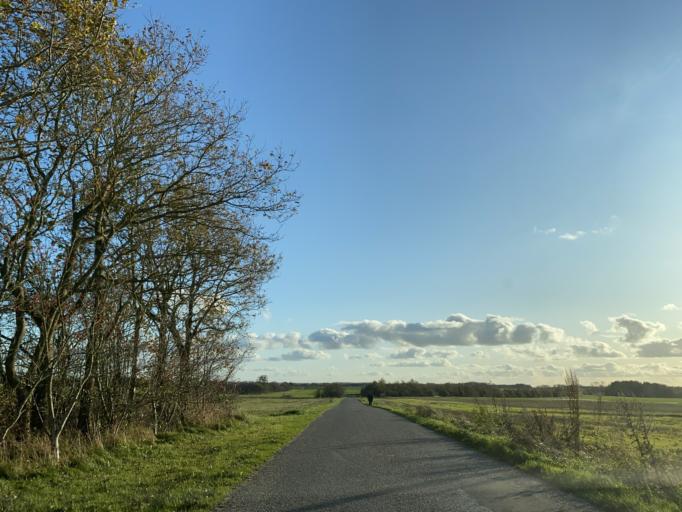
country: DK
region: Central Jutland
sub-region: Viborg Kommune
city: Bjerringbro
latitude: 56.3303
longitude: 9.7091
